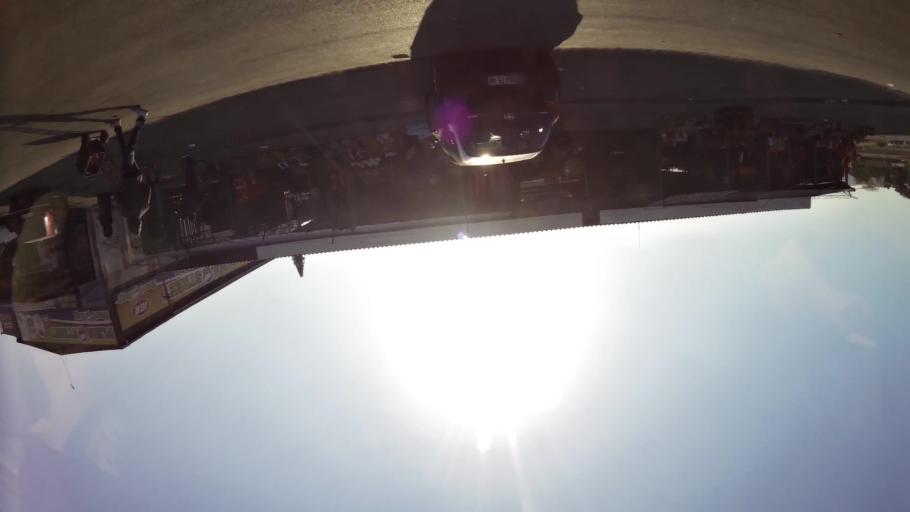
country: ZA
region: North-West
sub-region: Bojanala Platinum District Municipality
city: Rustenburg
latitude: -25.6494
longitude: 27.2388
